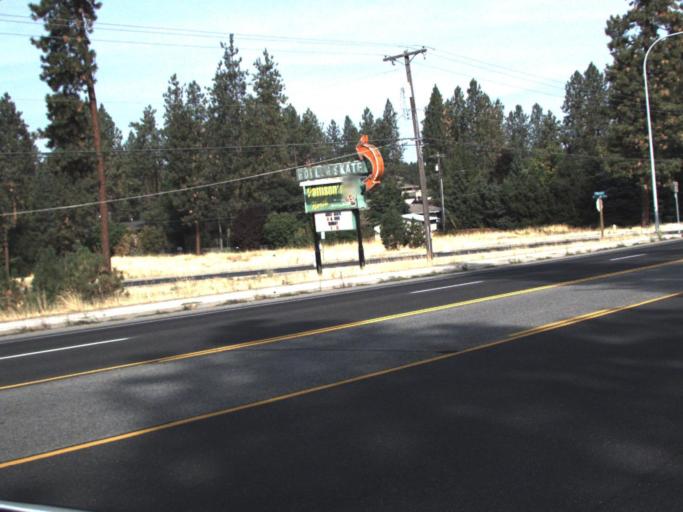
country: US
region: Washington
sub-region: Spokane County
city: Fairwood
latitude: 47.7609
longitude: -117.4075
